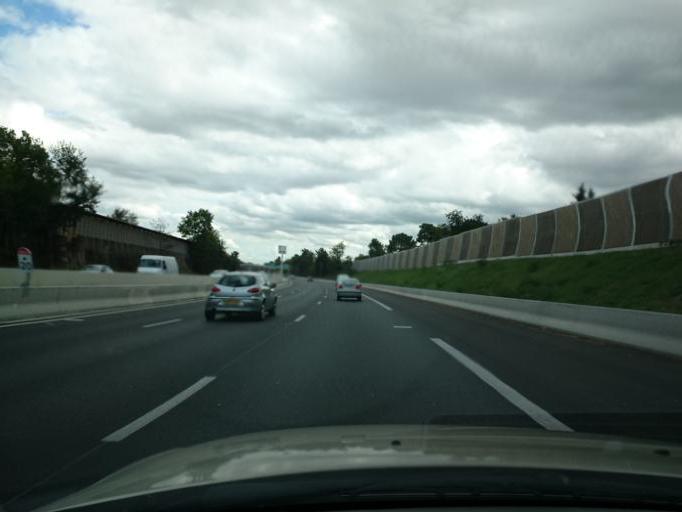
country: FR
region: Aquitaine
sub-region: Departement de la Gironde
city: Pessac
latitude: 44.8090
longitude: -0.6699
